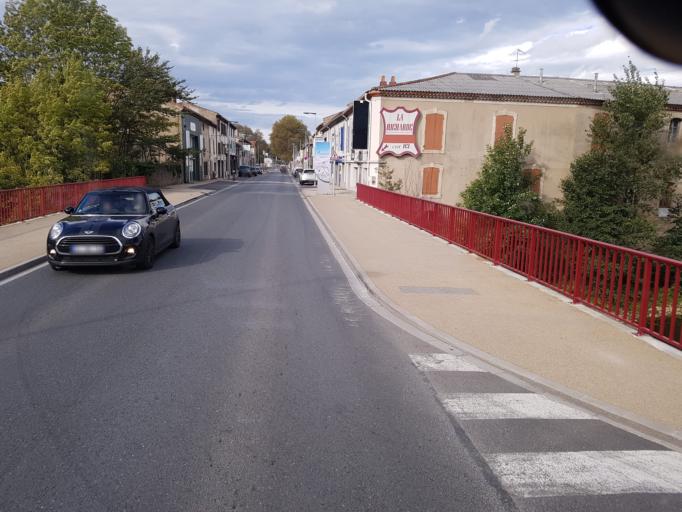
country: FR
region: Midi-Pyrenees
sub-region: Departement du Tarn
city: Pont-de-Larn
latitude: 43.4974
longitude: 2.3975
